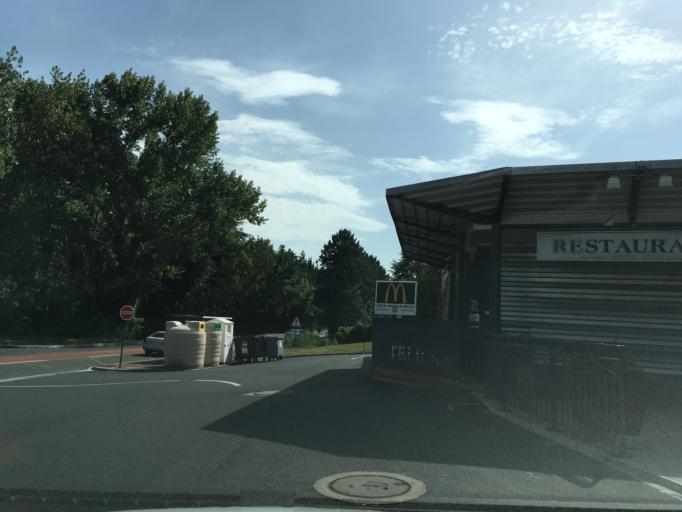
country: FR
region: Midi-Pyrenees
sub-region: Departement du Tarn
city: Castres
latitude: 43.6156
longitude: 2.2683
